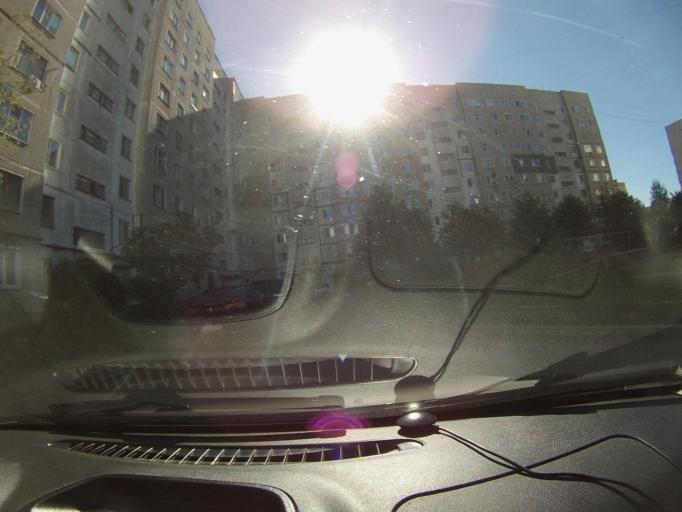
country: RU
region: Tambov
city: Tambov
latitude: 52.7687
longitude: 41.4105
